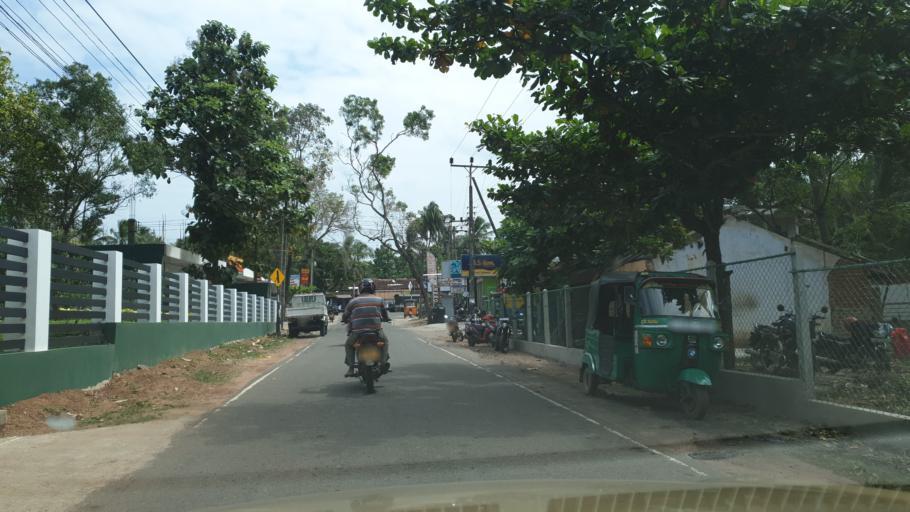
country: LK
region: North Western
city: Kuliyapitiya
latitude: 7.3475
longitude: 79.9839
